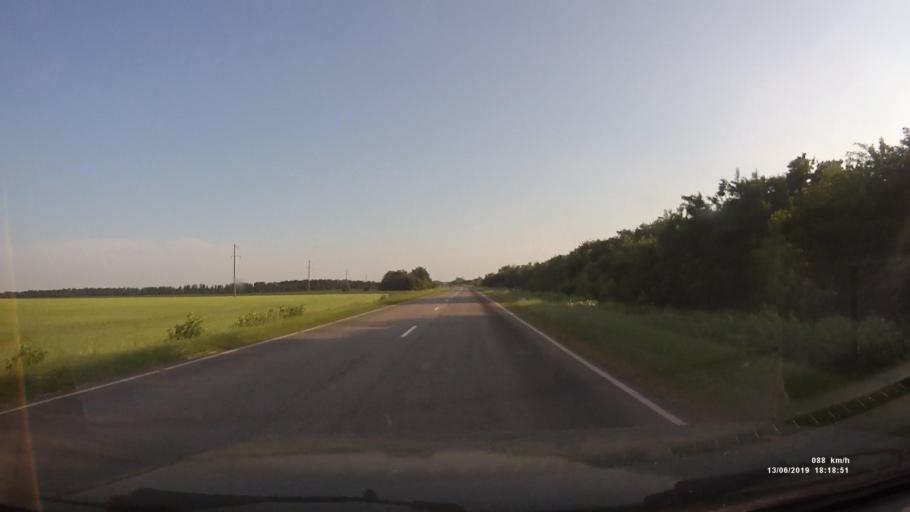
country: RU
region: Rostov
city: Kazanskaya
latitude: 49.9033
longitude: 41.3102
